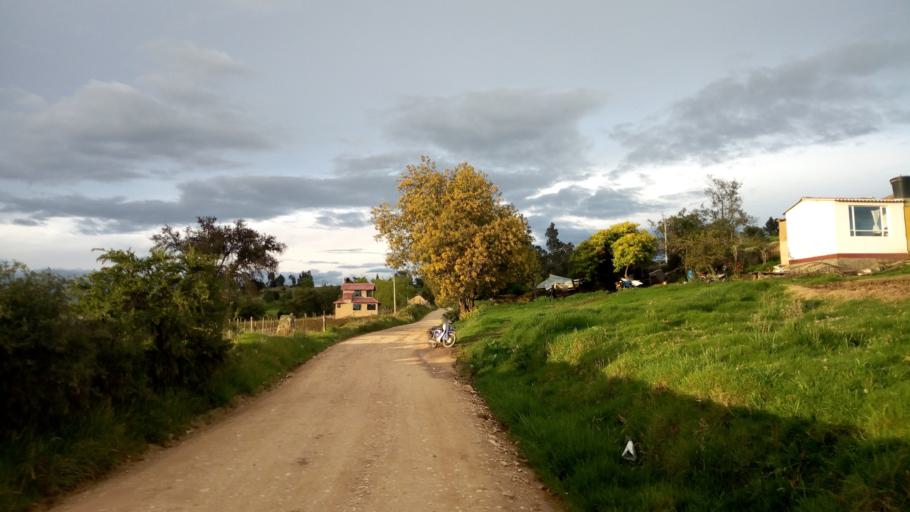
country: CO
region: Boyaca
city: Toca
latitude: 5.5786
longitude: -73.1777
